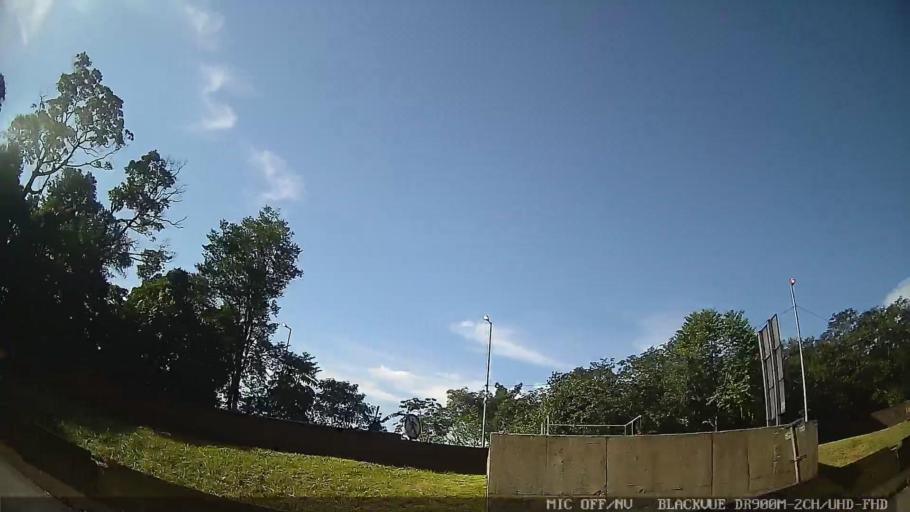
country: BR
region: Sao Paulo
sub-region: Cubatao
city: Cubatao
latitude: -23.8959
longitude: -46.4834
